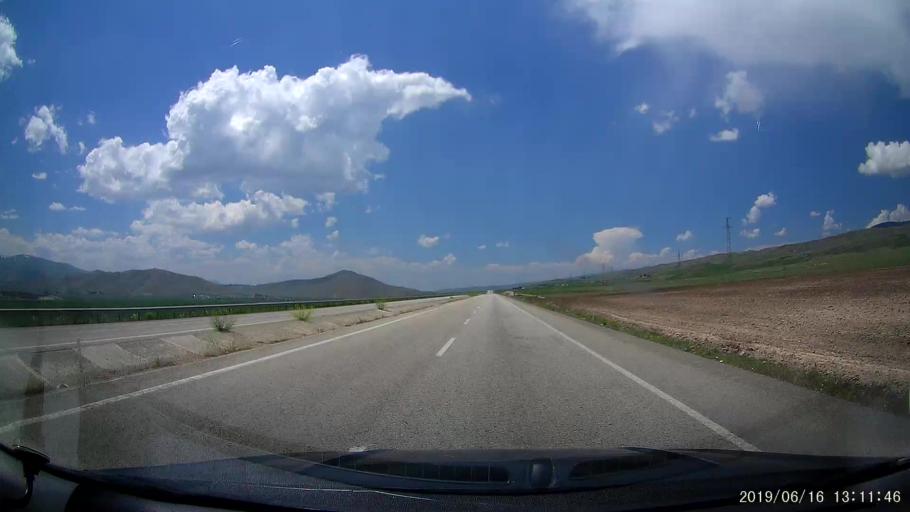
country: TR
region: Agri
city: Diyadin
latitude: 39.5935
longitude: 43.5983
